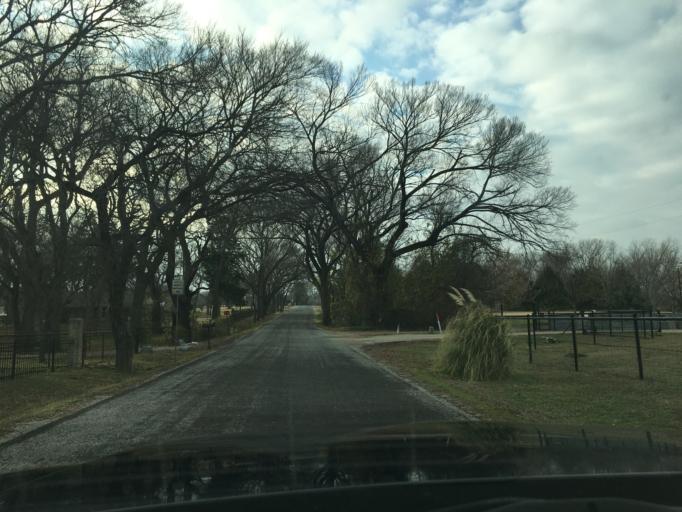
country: US
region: Texas
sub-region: Ellis County
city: Red Oak
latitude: 32.4791
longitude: -96.7844
